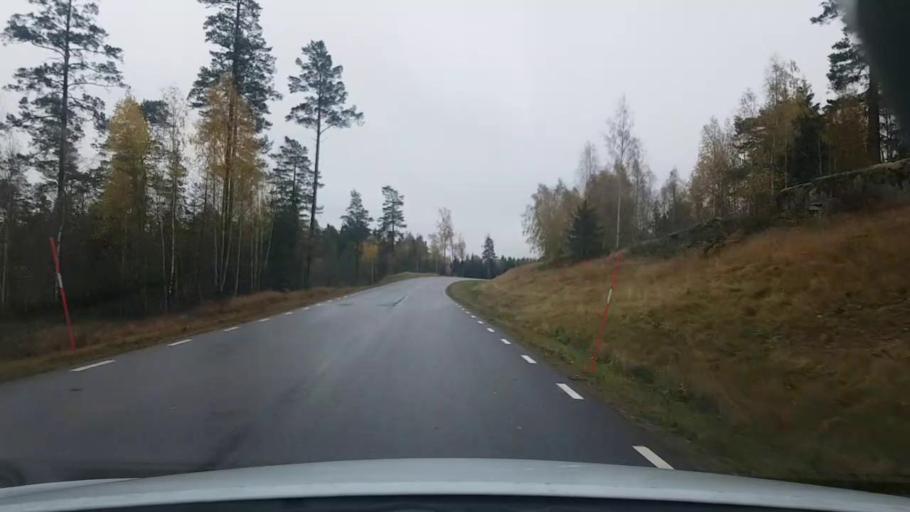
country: SE
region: Vaestra Goetaland
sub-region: Karlsborgs Kommun
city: Karlsborg
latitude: 58.6869
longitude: 14.5014
